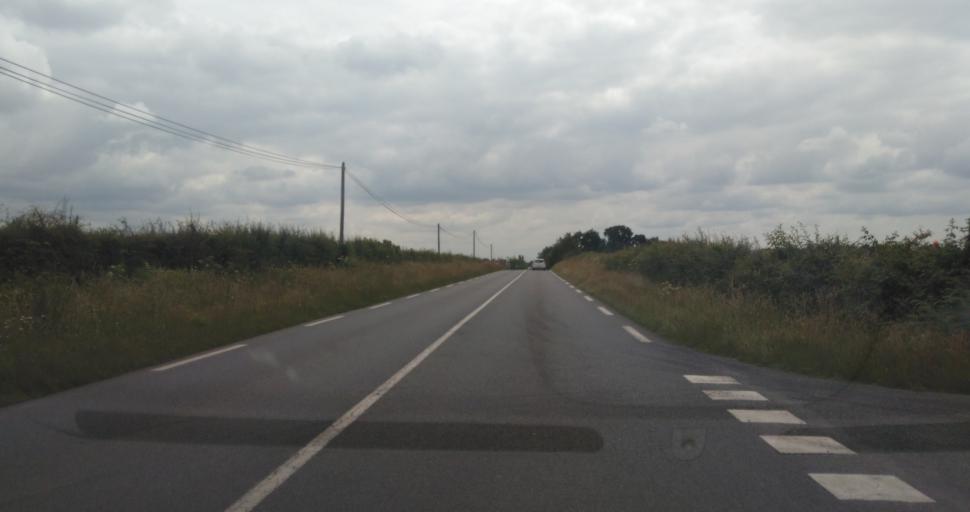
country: FR
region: Pays de la Loire
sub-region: Departement de la Vendee
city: Bournezeau
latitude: 46.6204
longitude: -1.1544
